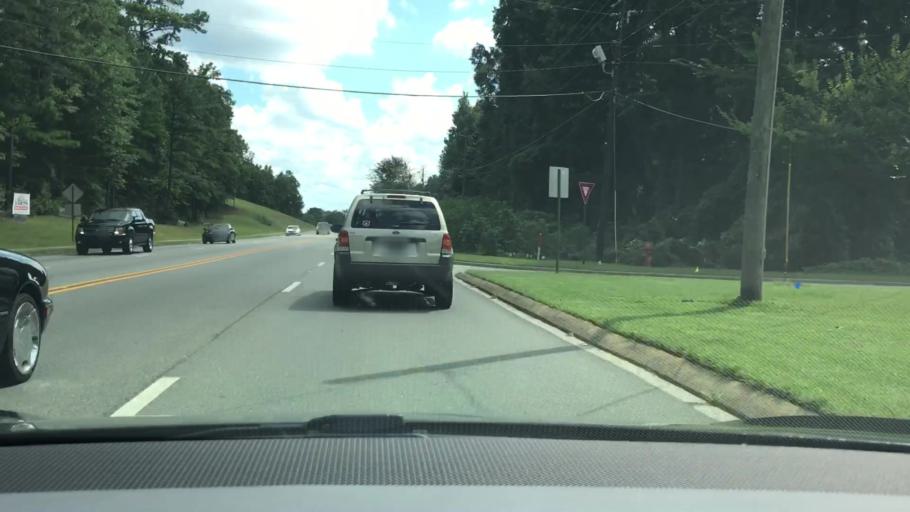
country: US
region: Alabama
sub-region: Lee County
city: Auburn
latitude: 32.6177
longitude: -85.4477
